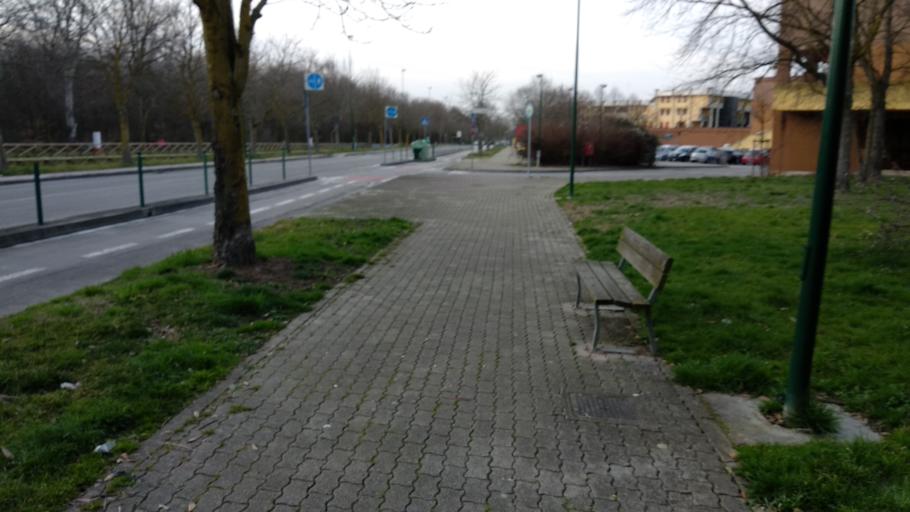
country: IT
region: Veneto
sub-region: Provincia di Venezia
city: Campalto
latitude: 45.4839
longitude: 12.2669
